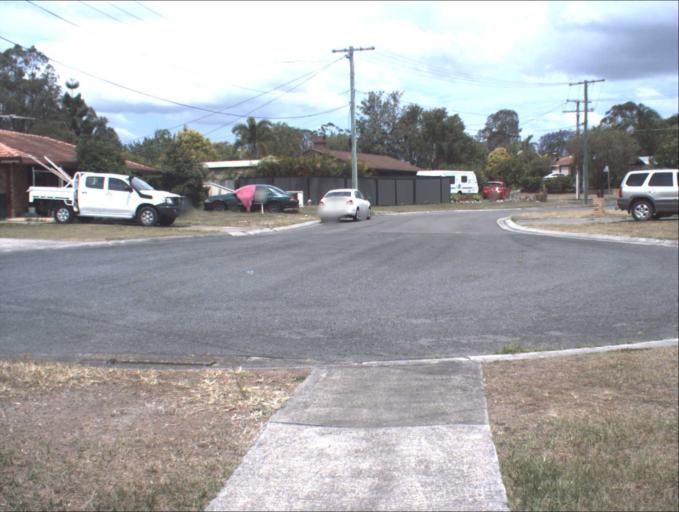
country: AU
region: Queensland
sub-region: Logan
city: Waterford West
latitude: -27.6966
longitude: 153.1645
